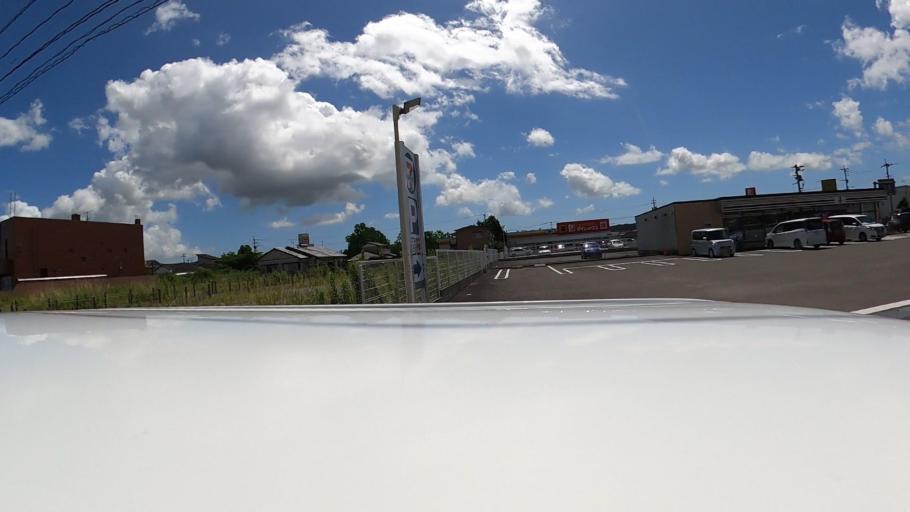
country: JP
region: Miyazaki
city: Tsuma
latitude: 32.1046
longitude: 131.3999
